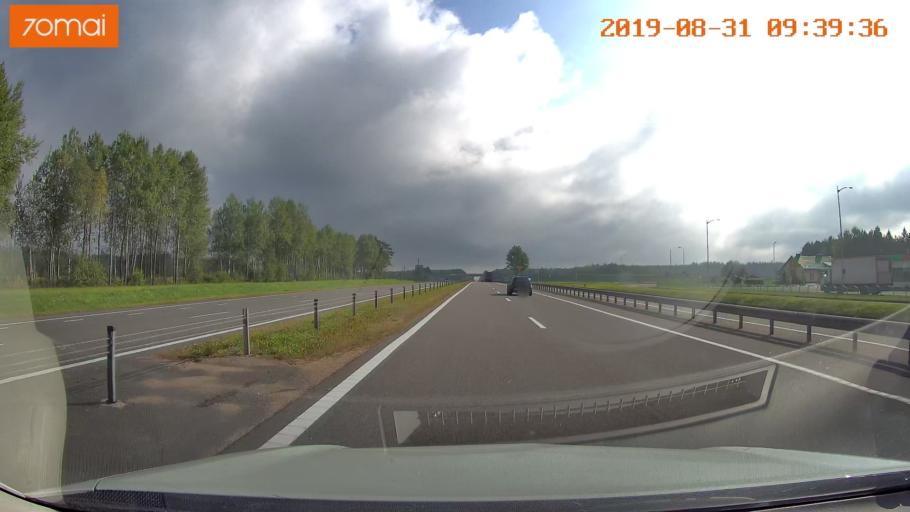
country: BY
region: Mogilev
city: Byalynichy
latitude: 53.9063
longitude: 29.3986
